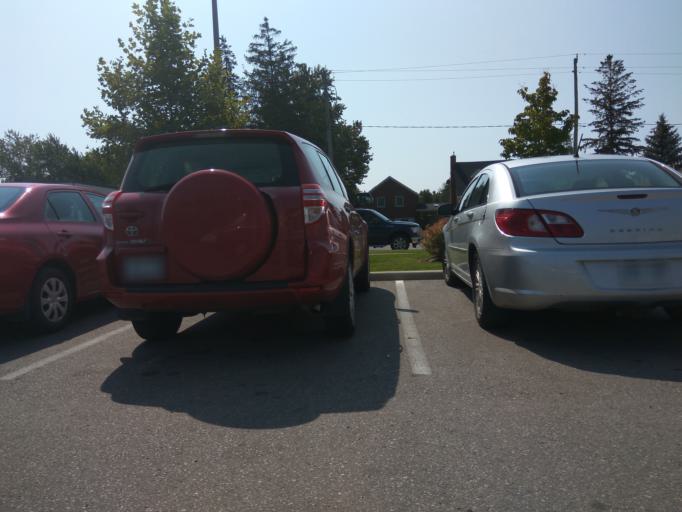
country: CA
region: Ontario
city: Stratford
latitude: 43.3818
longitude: -81.0047
